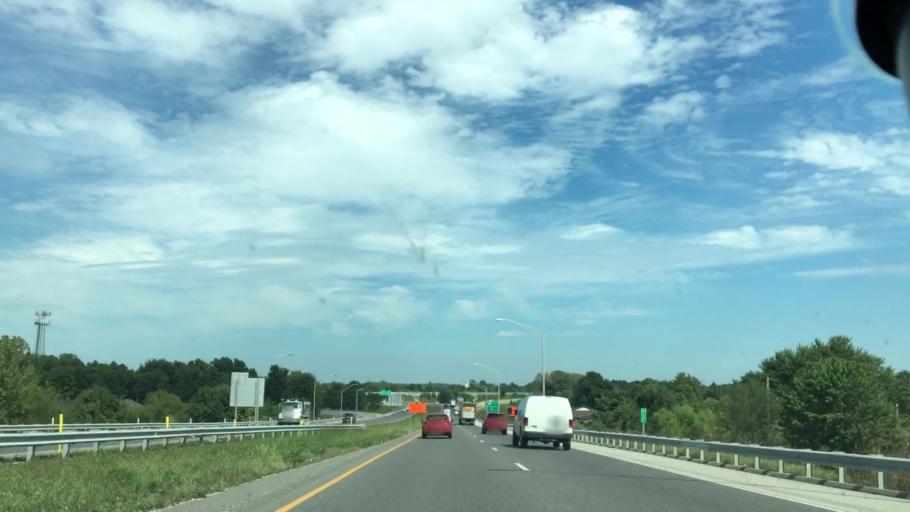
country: US
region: Kentucky
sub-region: Daviess County
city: Owensboro
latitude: 37.7359
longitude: -87.0804
